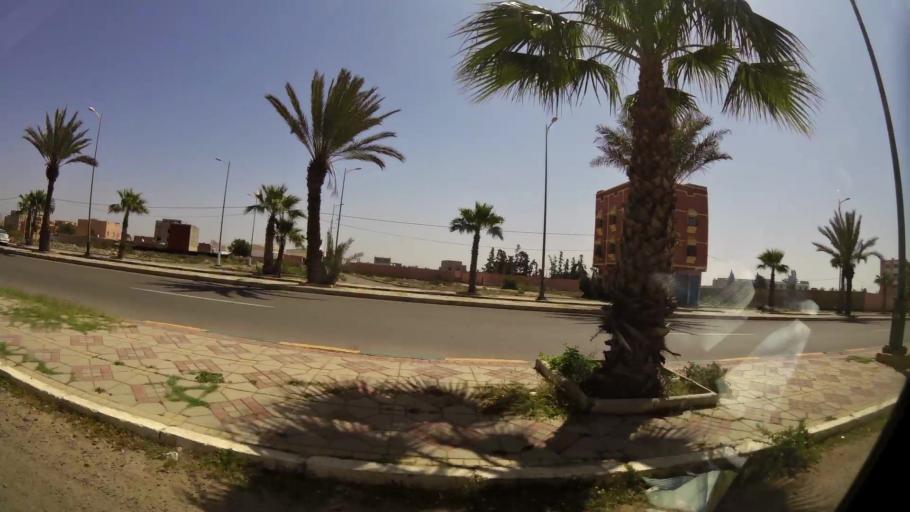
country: MA
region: Souss-Massa-Draa
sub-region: Inezgane-Ait Mellou
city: Inezgane
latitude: 30.3186
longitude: -9.5033
